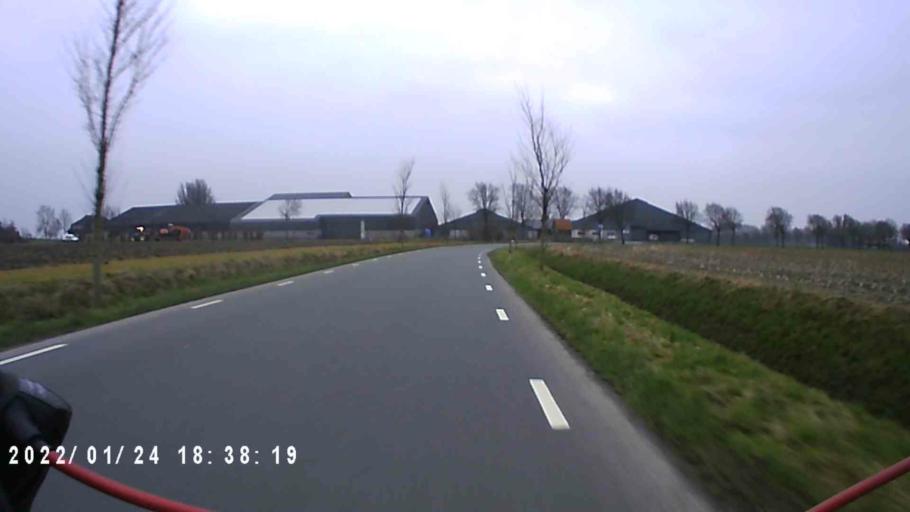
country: NL
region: Groningen
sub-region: Gemeente De Marne
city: Ulrum
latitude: 53.3487
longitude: 6.3357
